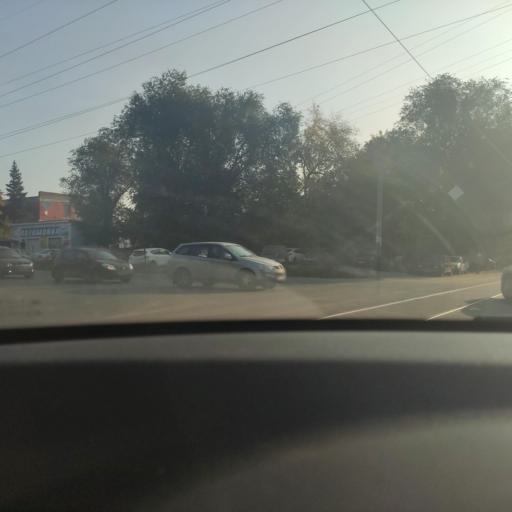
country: RU
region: Samara
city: Petra-Dubrava
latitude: 53.2381
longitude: 50.2875
